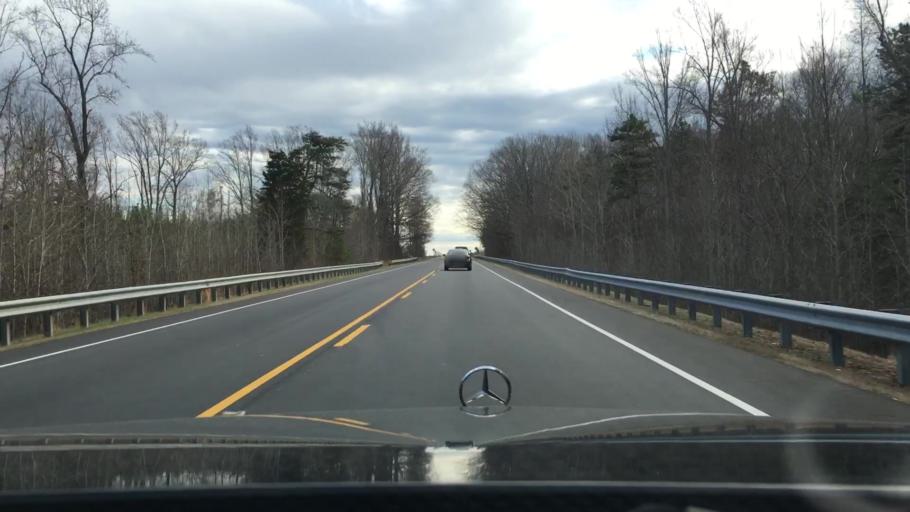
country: US
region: North Carolina
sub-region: Caswell County
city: Yanceyville
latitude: 36.4357
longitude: -79.3608
